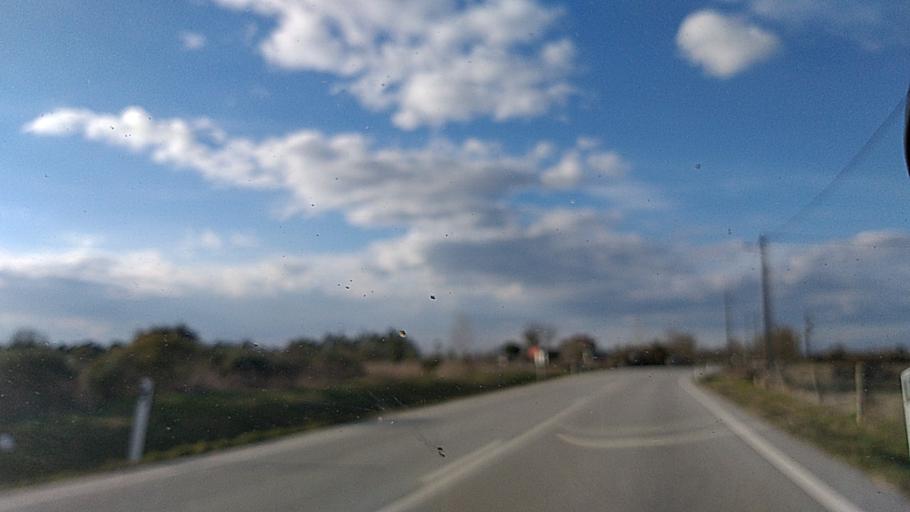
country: ES
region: Castille and Leon
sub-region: Provincia de Salamanca
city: Fuentes de Onoro
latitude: 40.6318
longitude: -6.8536
